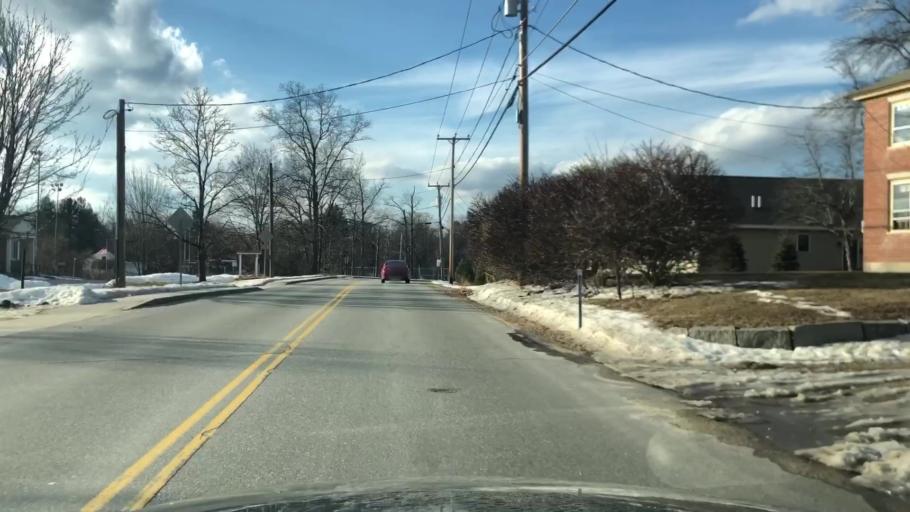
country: US
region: New Hampshire
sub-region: Hillsborough County
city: Milford
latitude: 42.8413
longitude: -71.6593
